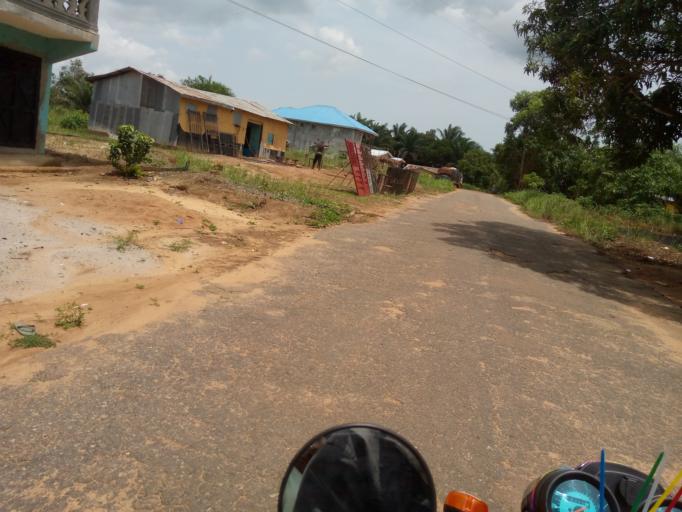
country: SL
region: Western Area
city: Waterloo
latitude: 8.3421
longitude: -12.9857
